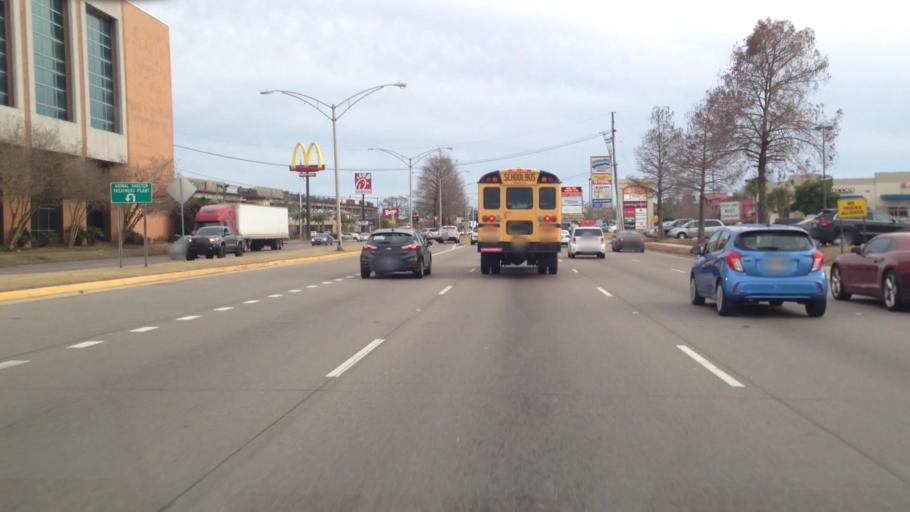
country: US
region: Louisiana
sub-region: Jefferson Parish
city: Elmwood
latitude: 29.9628
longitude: -90.1849
